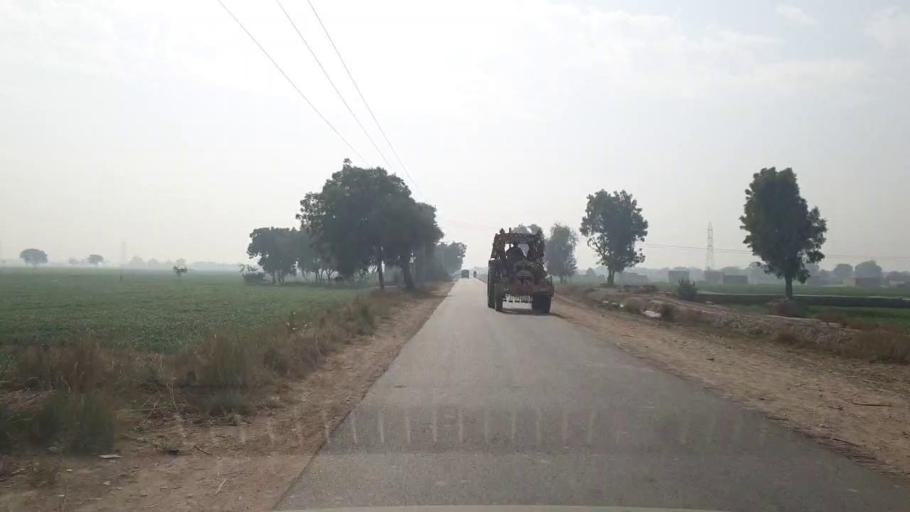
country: PK
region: Sindh
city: Hala
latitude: 25.8037
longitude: 68.4366
